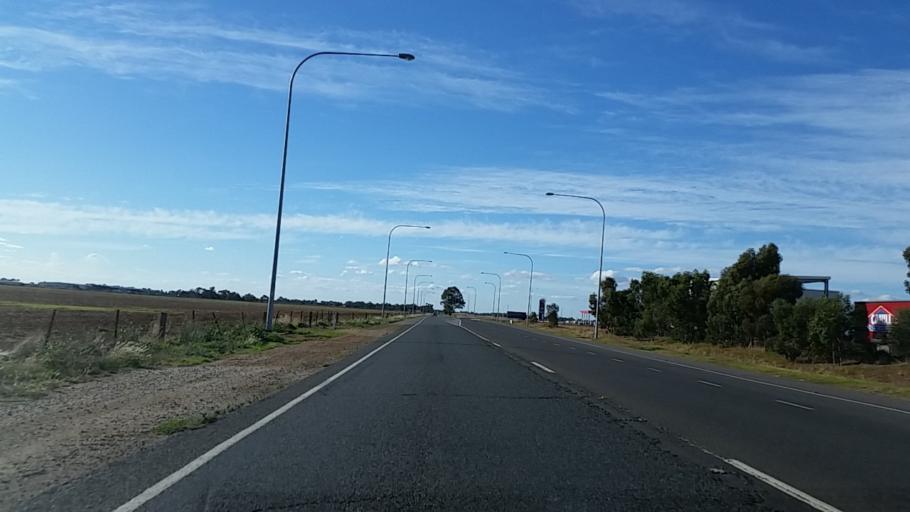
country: AU
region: South Australia
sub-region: Salisbury
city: Salisbury
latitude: -34.7180
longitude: 138.5997
